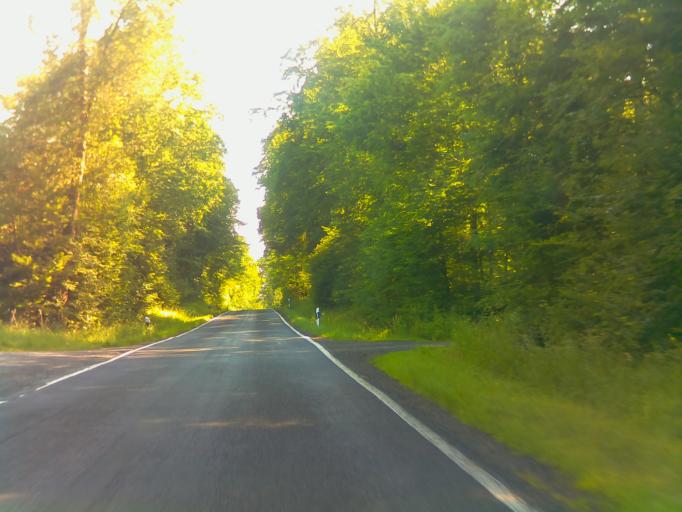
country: DE
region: Hesse
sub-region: Regierungsbezirk Giessen
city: Lich
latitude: 50.5474
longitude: 8.8395
